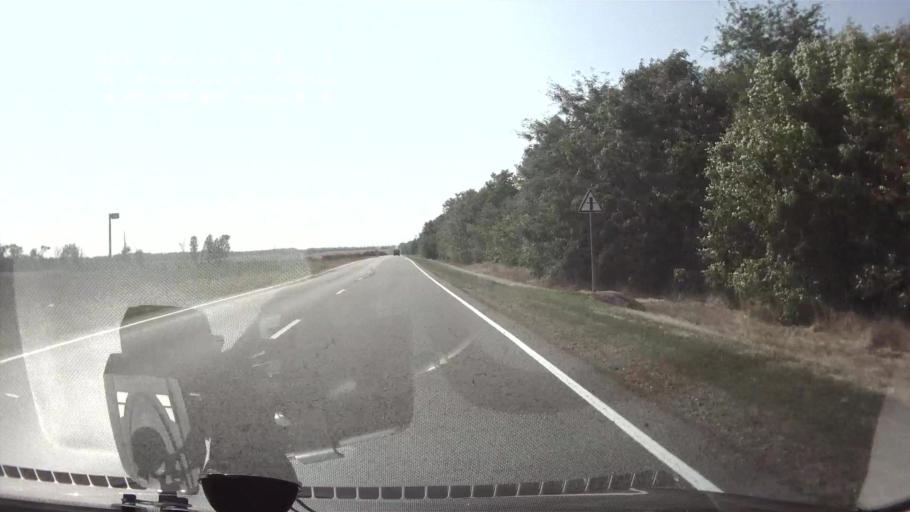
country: RU
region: Krasnodarskiy
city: Novopokrovskaya
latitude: 45.8565
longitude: 40.7206
